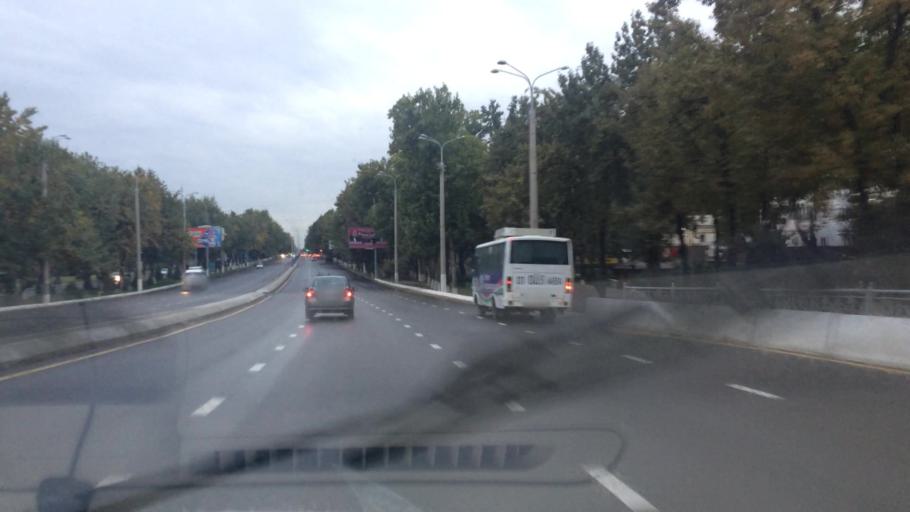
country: UZ
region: Toshkent Shahri
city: Tashkent
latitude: 41.2731
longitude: 69.2035
